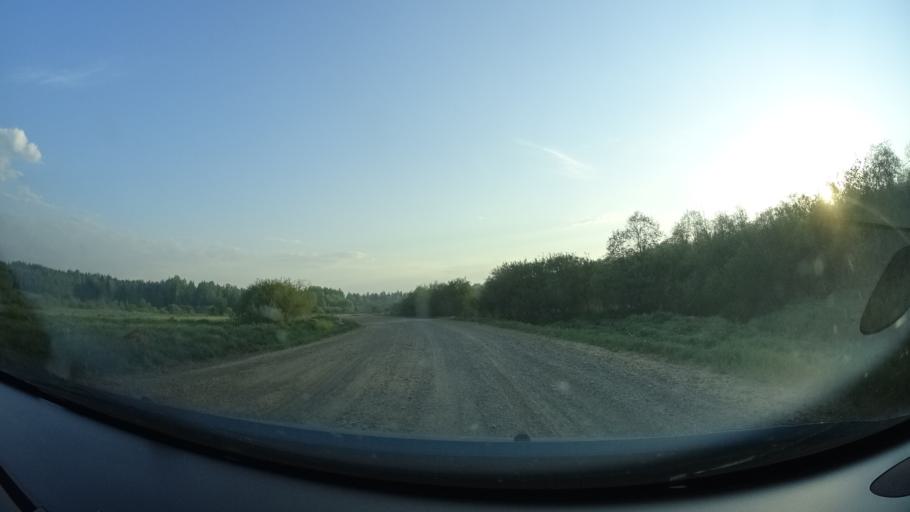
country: RU
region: Perm
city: Kuyeda
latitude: 56.6181
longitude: 55.7106
